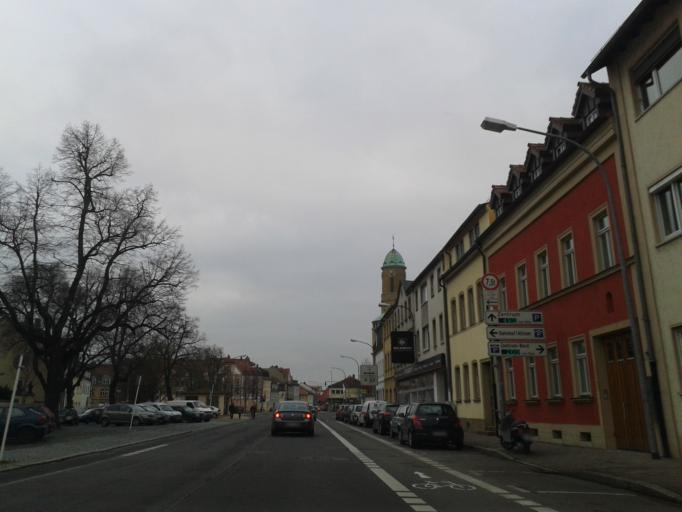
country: DE
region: Bavaria
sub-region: Upper Franconia
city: Bamberg
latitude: 49.9034
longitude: 10.8875
